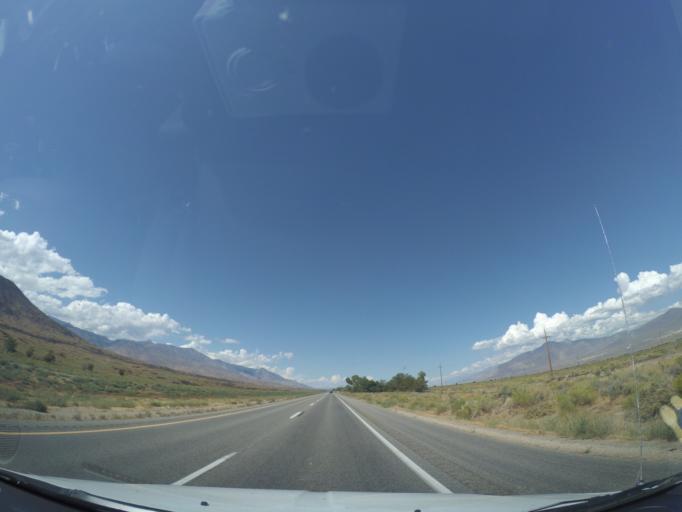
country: US
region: California
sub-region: Inyo County
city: Big Pine
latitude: 37.1143
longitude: -118.2576
